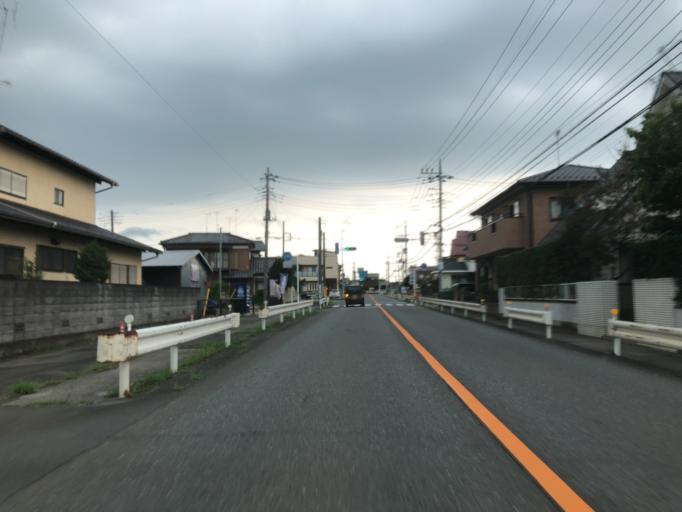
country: JP
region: Saitama
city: Sakado
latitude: 36.0251
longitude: 139.3924
